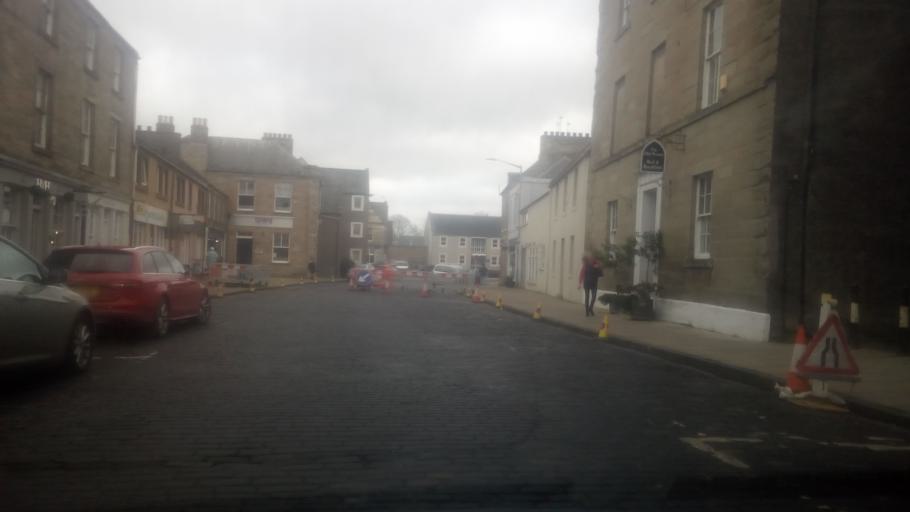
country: GB
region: Scotland
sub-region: The Scottish Borders
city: Kelso
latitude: 55.5989
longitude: -2.4323
